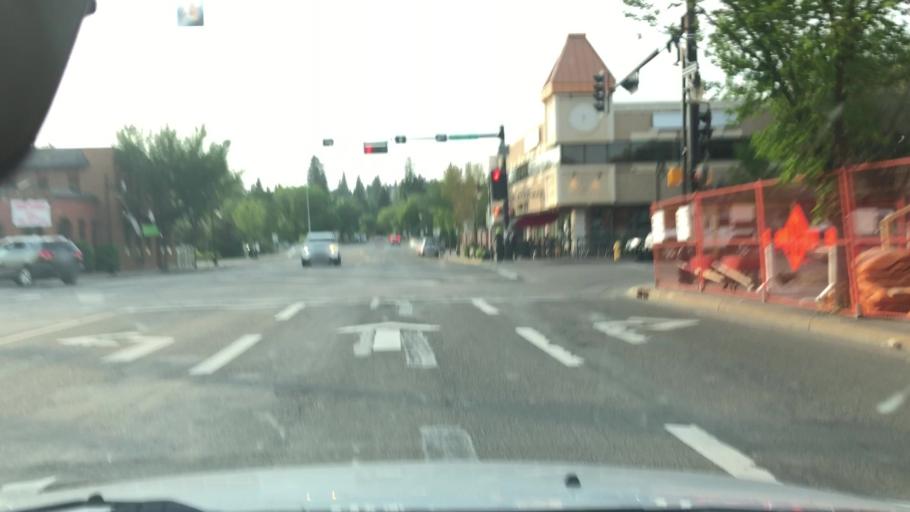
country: CA
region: Alberta
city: St. Albert
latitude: 53.6345
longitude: -113.6260
